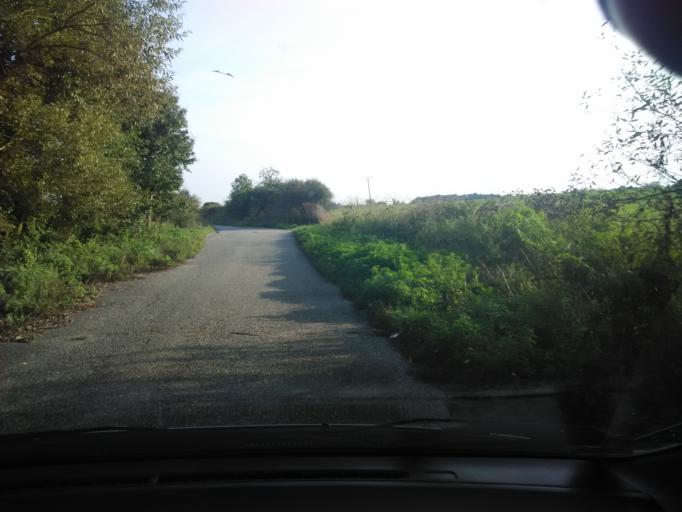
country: SK
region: Nitriansky
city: Levice
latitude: 48.3000
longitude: 18.7000
